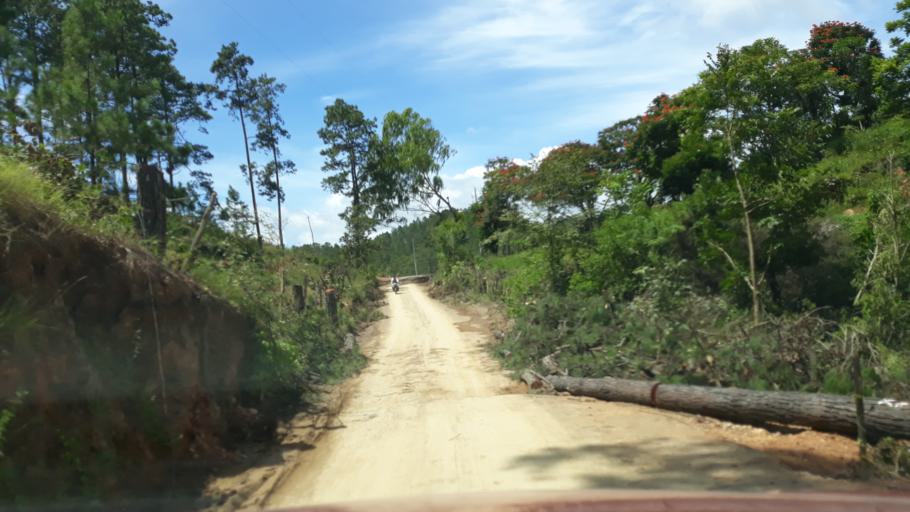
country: HN
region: El Paraiso
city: Santa Cruz
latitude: 13.7542
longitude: -86.6593
